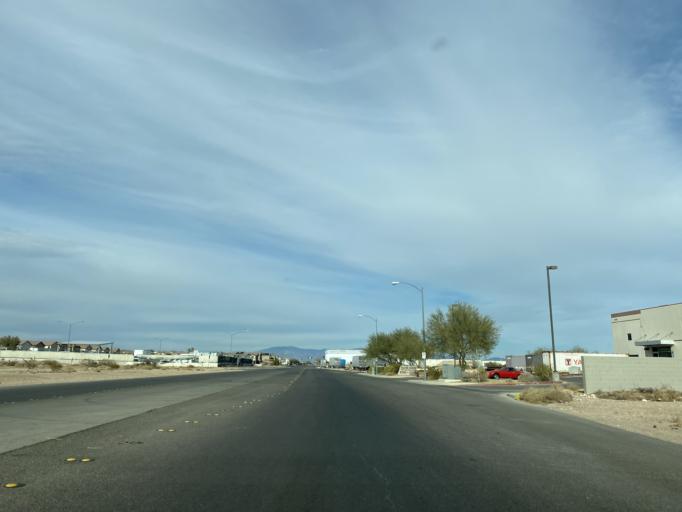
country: US
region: Nevada
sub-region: Clark County
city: Enterprise
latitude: 36.0302
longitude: -115.2257
